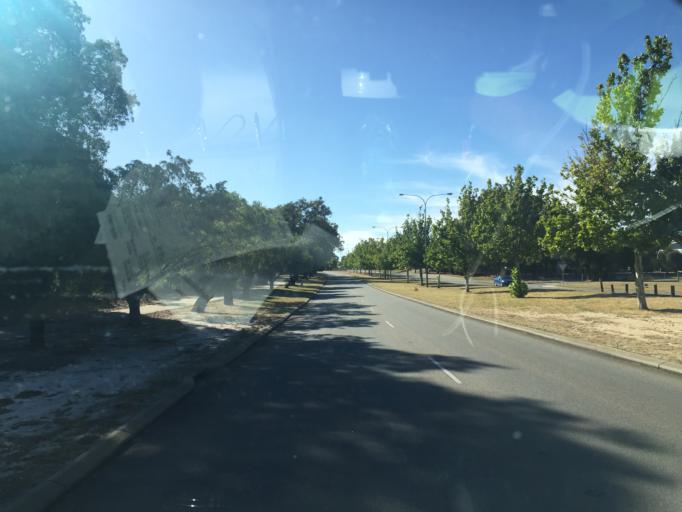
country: AU
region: Western Australia
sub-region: Canning
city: East Cannington
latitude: -31.9977
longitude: 115.9621
